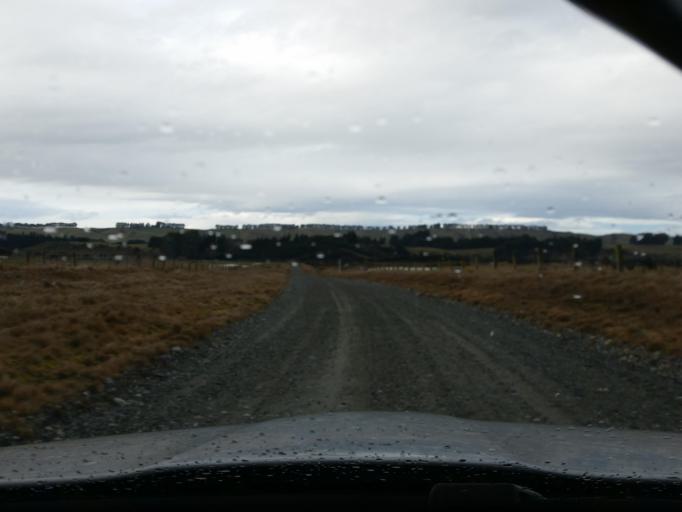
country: NZ
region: Southland
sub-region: Southland District
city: Te Anau
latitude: -45.4705
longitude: 167.6893
